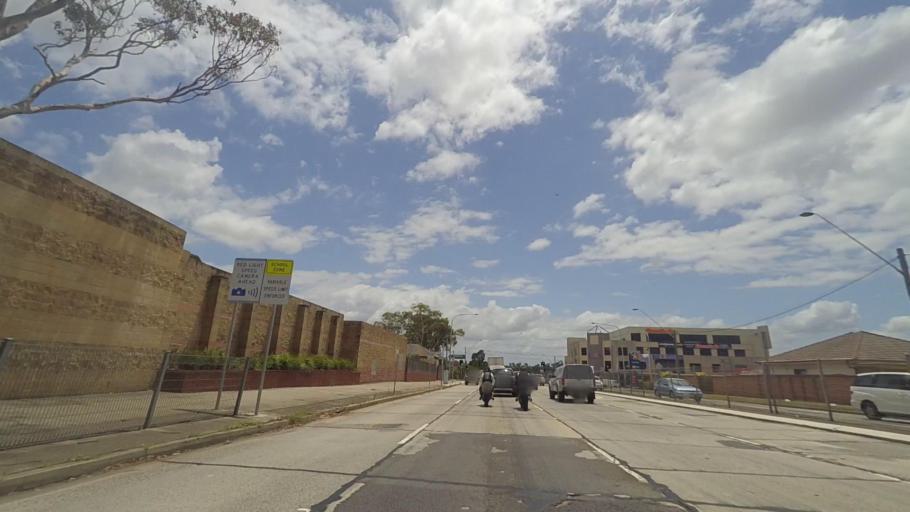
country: AU
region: New South Wales
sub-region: Fairfield
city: Cabramatta West
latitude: -33.8845
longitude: 150.9236
